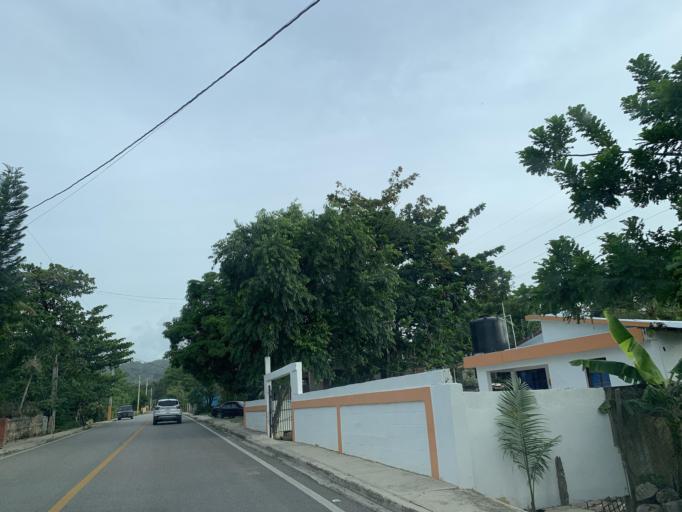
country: DO
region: Puerto Plata
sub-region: Puerto Plata
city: Puerto Plata
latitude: 19.7023
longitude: -70.6244
